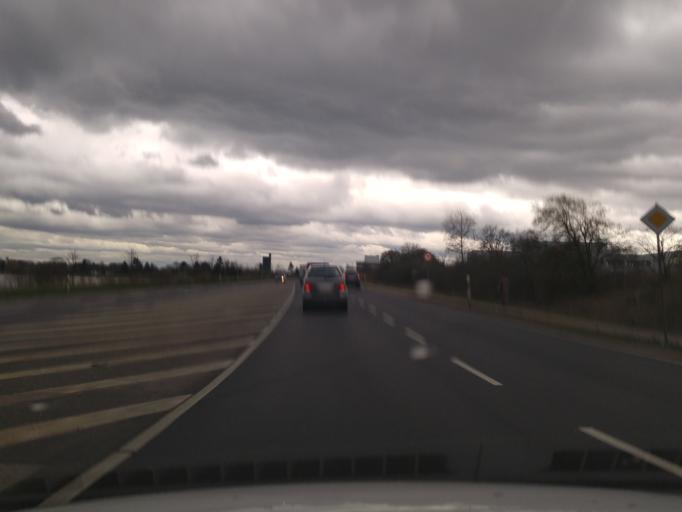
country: DE
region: North Rhine-Westphalia
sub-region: Regierungsbezirk Dusseldorf
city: Dusseldorf
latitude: 51.1626
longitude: 6.7697
